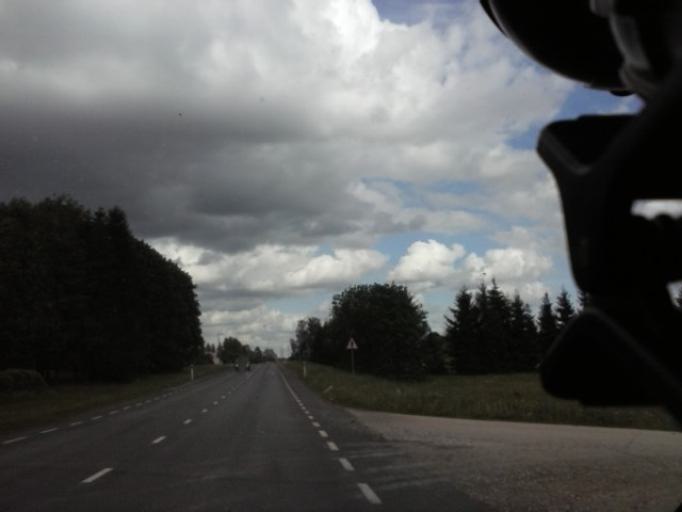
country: EE
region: Jogevamaa
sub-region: Poltsamaa linn
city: Poltsamaa
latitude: 58.6404
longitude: 25.8872
